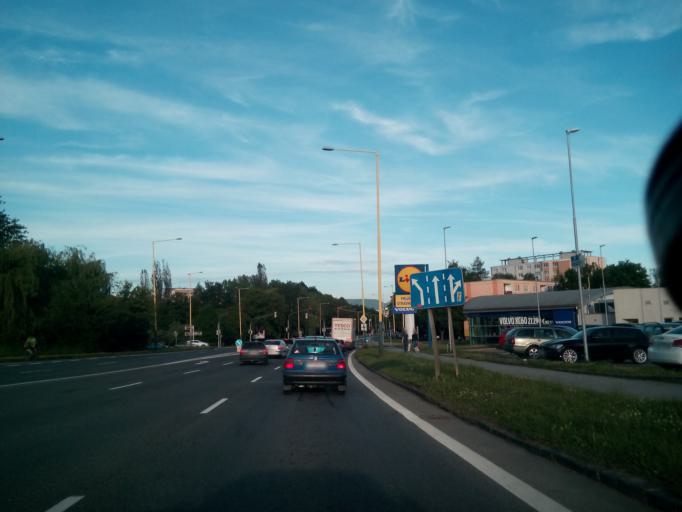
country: SK
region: Presovsky
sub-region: Okres Presov
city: Presov
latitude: 49.0023
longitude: 21.2189
